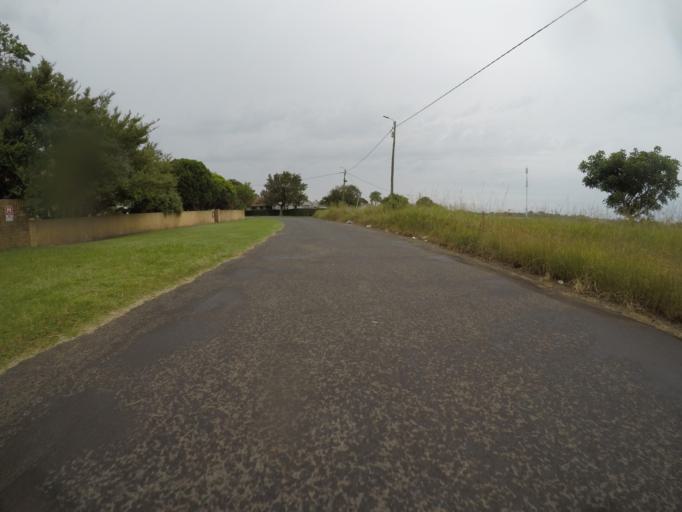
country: ZA
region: Eastern Cape
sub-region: Buffalo City Metropolitan Municipality
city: East London
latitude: -32.9686
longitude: 27.8301
